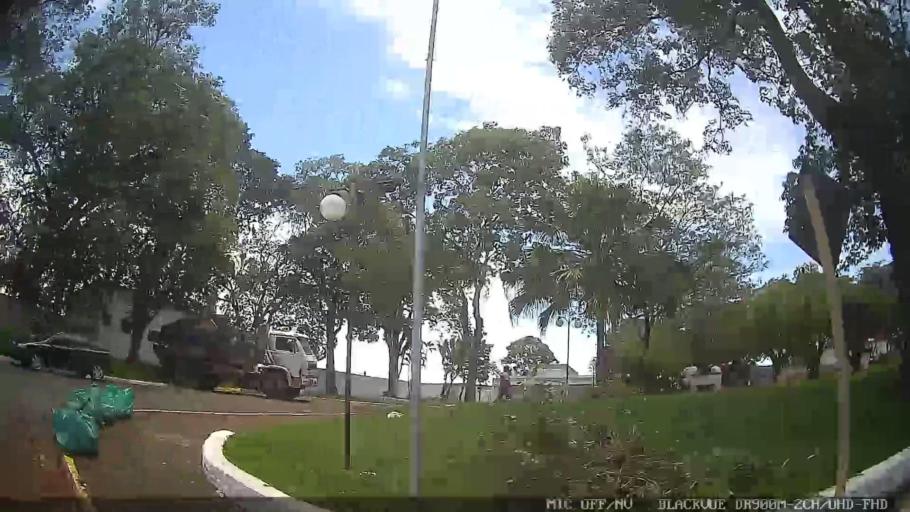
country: BR
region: Sao Paulo
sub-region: Laranjal Paulista
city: Laranjal Paulista
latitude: -23.0517
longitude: -47.8302
